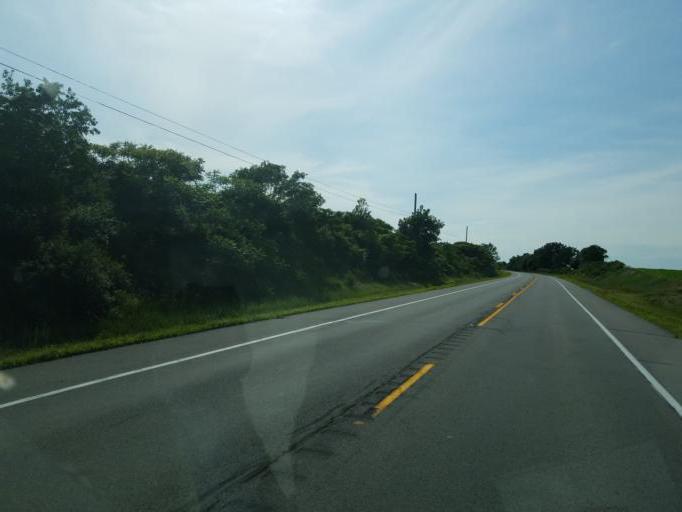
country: US
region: New York
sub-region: Livingston County
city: Avon
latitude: 42.9346
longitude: -77.7983
